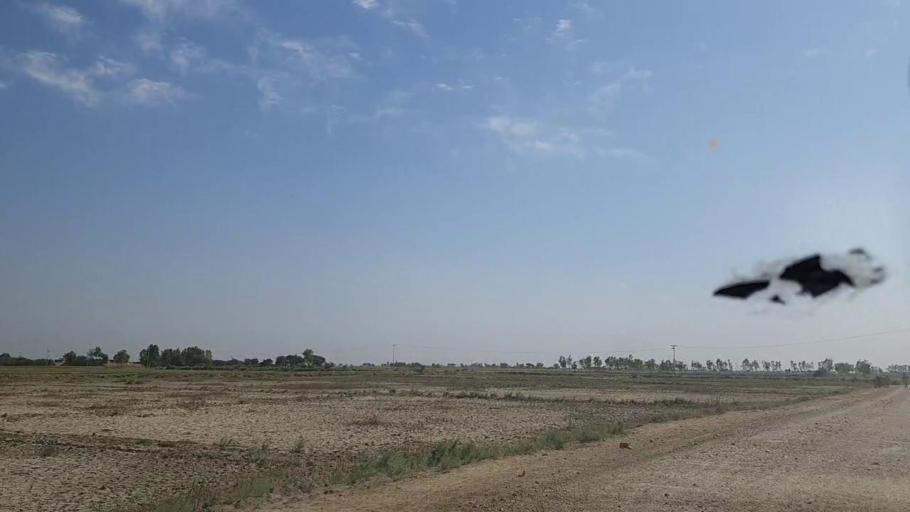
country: PK
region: Sindh
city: Daro Mehar
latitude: 24.6656
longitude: 68.0810
